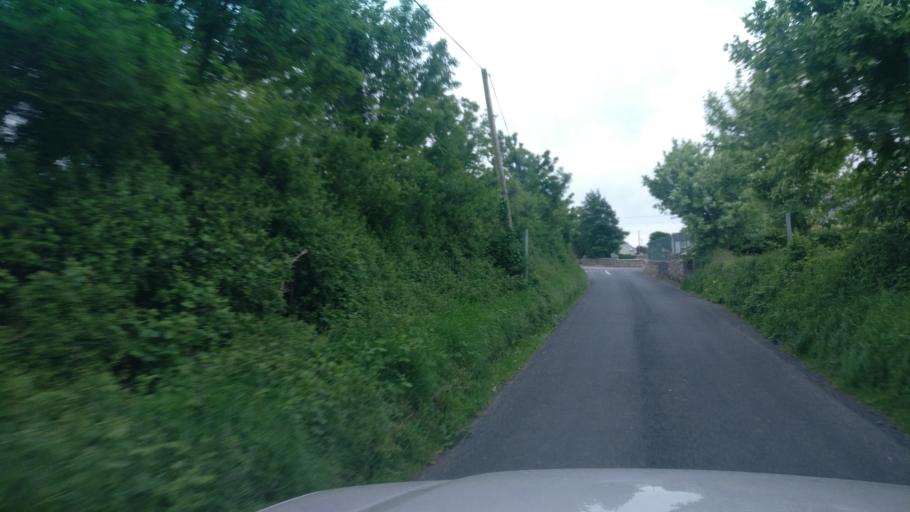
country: IE
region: Connaught
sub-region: County Galway
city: Portumna
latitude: 53.1131
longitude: -8.2875
